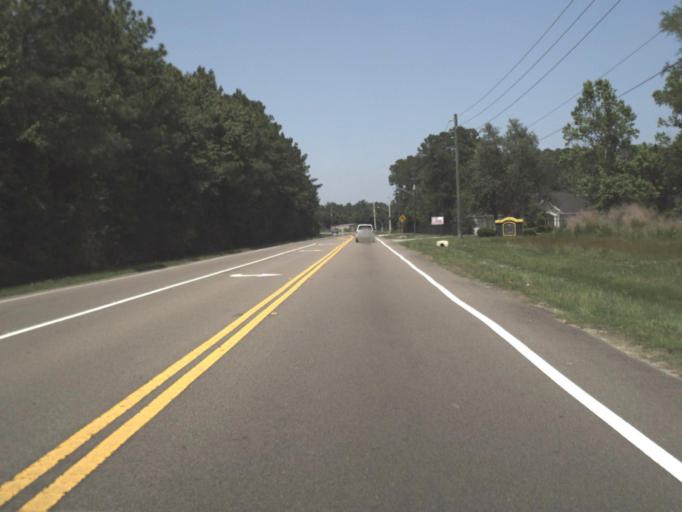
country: US
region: Florida
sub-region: Nassau County
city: Yulee
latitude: 30.4925
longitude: -81.6242
